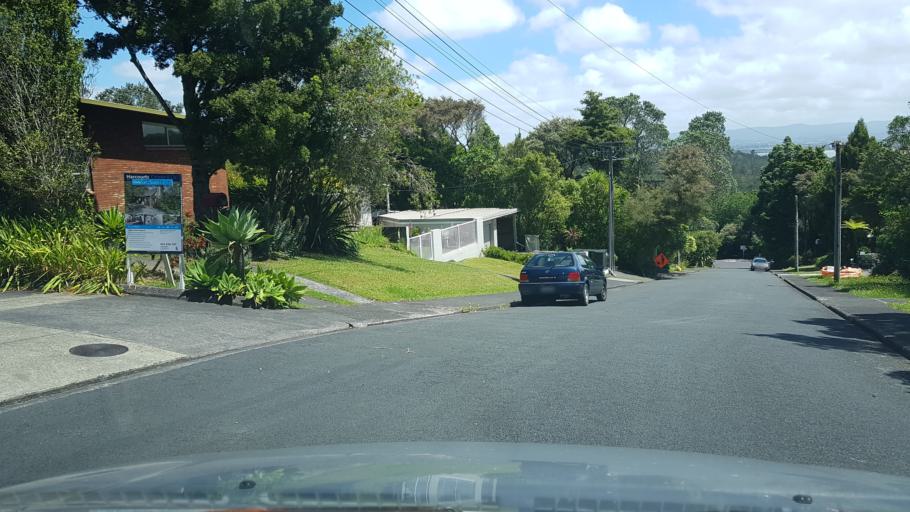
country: NZ
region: Auckland
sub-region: Auckland
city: North Shore
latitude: -36.8091
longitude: 174.7062
